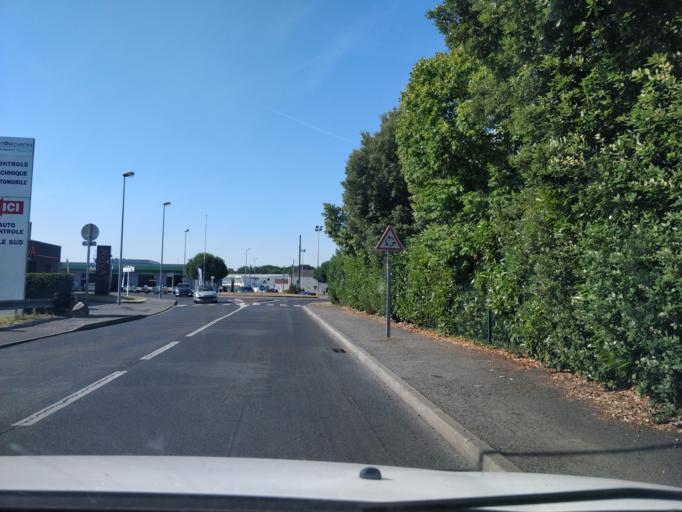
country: FR
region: Pays de la Loire
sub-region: Departement de la Loire-Atlantique
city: Vertou
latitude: 47.1878
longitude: -1.4640
